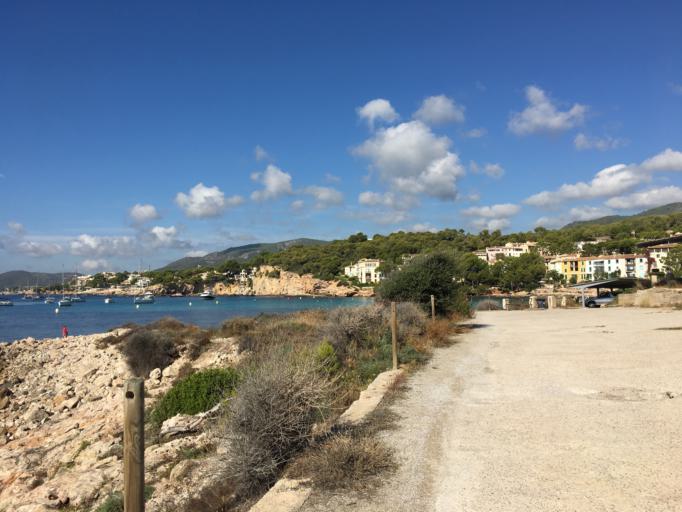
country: ES
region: Balearic Islands
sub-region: Illes Balears
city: Magaluf
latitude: 39.5318
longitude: 2.5900
